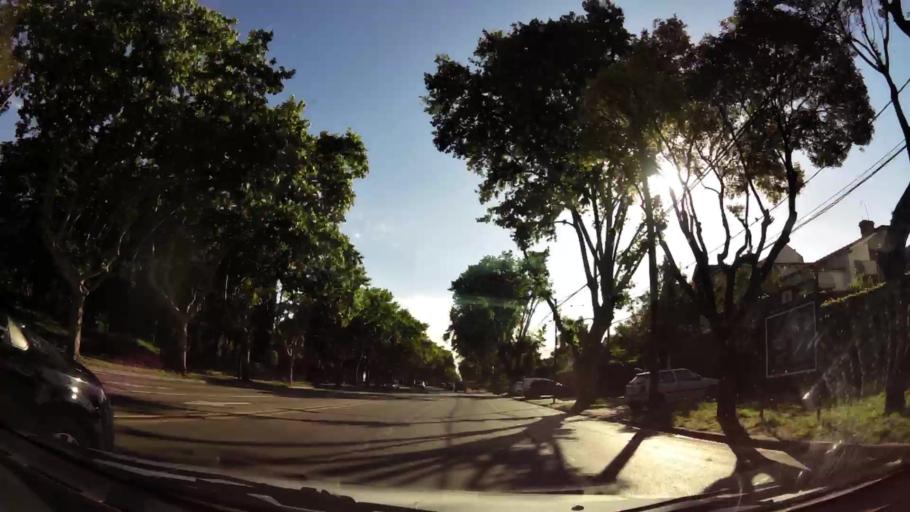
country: AR
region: Buenos Aires
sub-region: Partido de San Isidro
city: San Isidro
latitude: -34.4768
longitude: -58.5174
